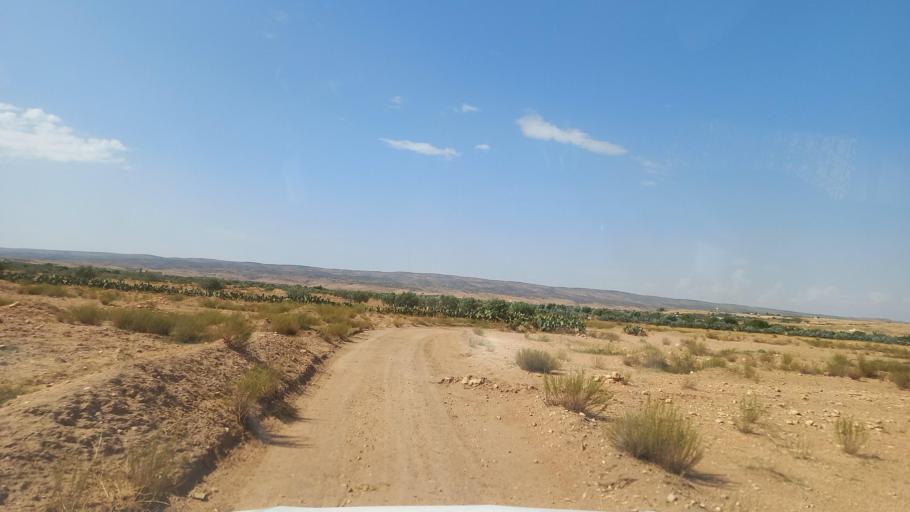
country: TN
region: Al Qasrayn
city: Kasserine
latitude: 35.2564
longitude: 8.9549
